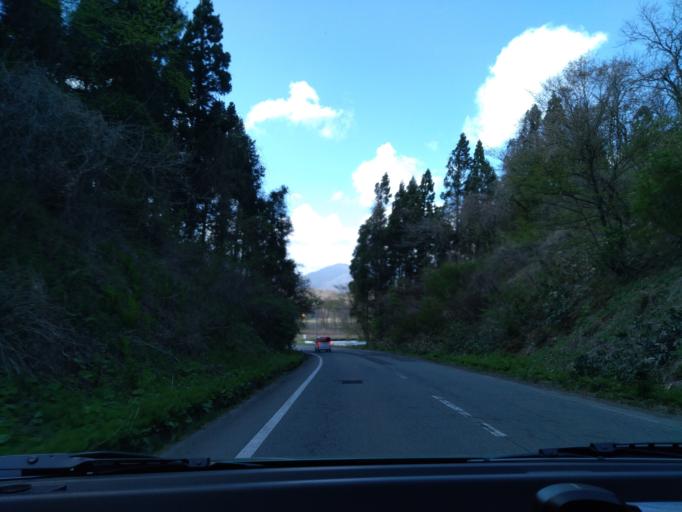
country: JP
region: Akita
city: Akita
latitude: 39.6918
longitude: 140.2747
